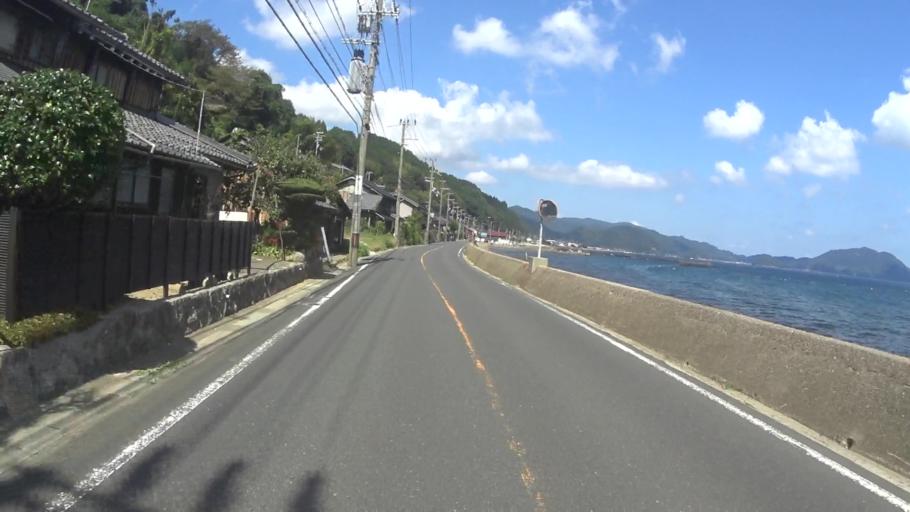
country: JP
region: Kyoto
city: Miyazu
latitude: 35.6466
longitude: 135.2516
